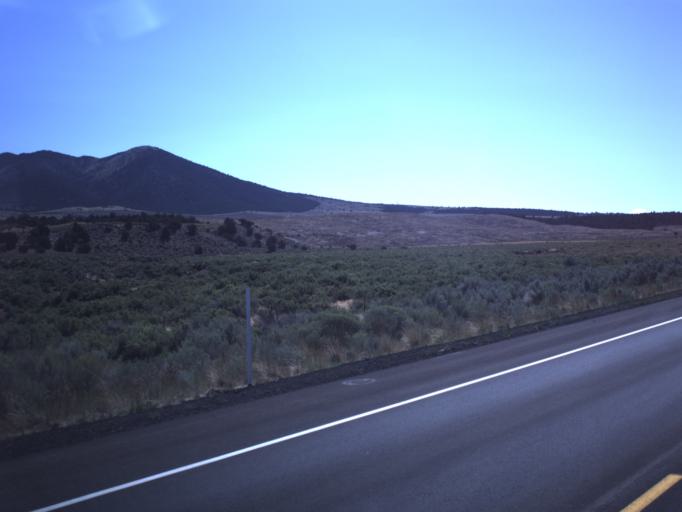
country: US
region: Utah
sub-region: Utah County
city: Eagle Mountain
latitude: 40.0154
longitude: -112.2782
